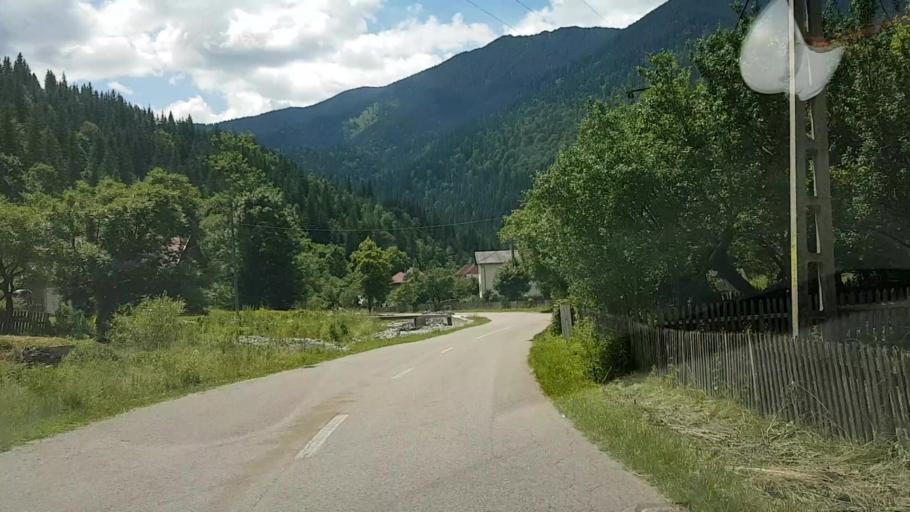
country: RO
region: Suceava
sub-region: Comuna Crucea
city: Crucea
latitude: 47.4014
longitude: 25.5703
